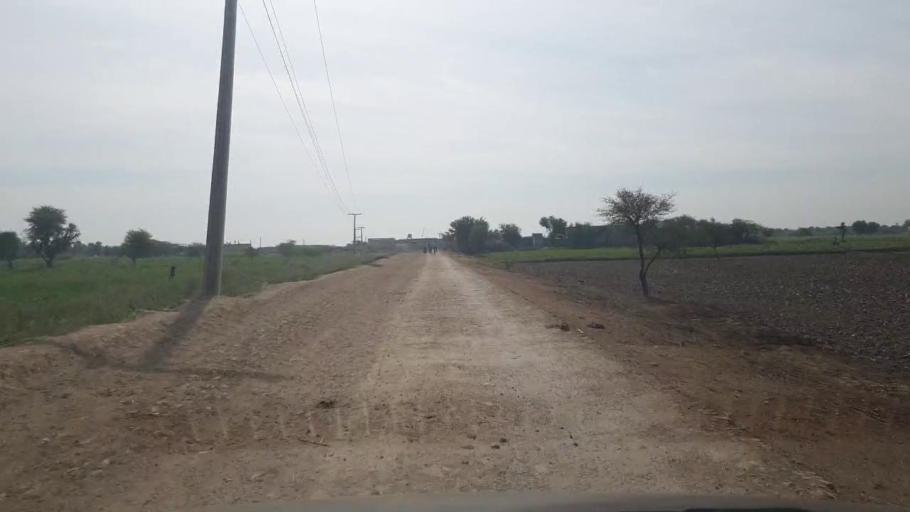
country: PK
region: Sindh
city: Umarkot
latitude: 25.3585
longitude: 69.6278
